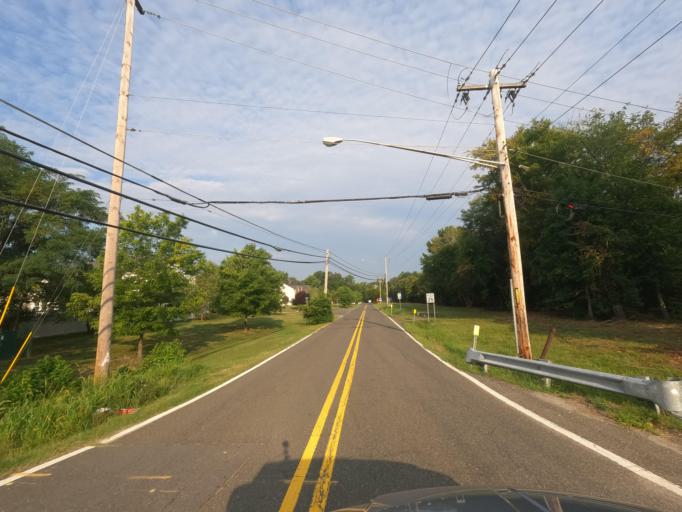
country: US
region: Maryland
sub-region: Prince George's County
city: Fort Washington
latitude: 38.6855
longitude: -76.9965
